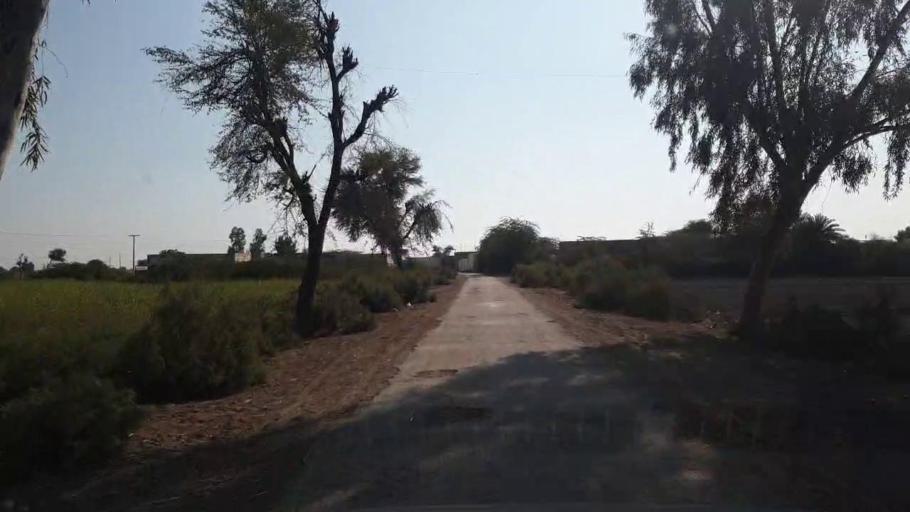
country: PK
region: Sindh
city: Shahpur Chakar
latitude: 26.1532
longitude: 68.6710
